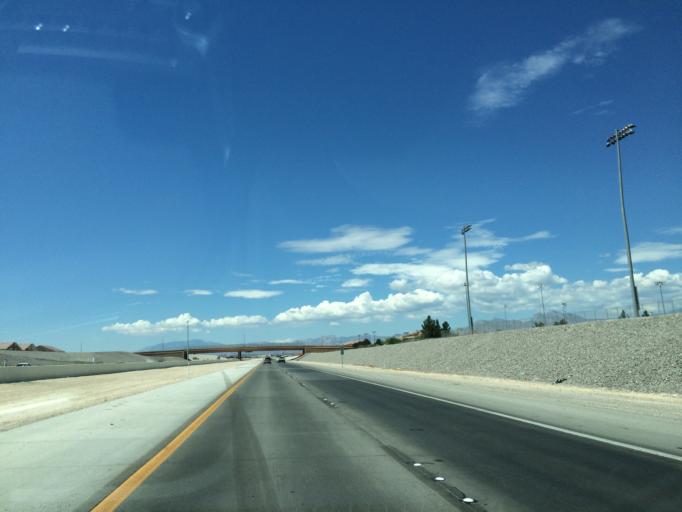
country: US
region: Nevada
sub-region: Clark County
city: North Las Vegas
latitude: 36.2841
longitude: -115.1877
